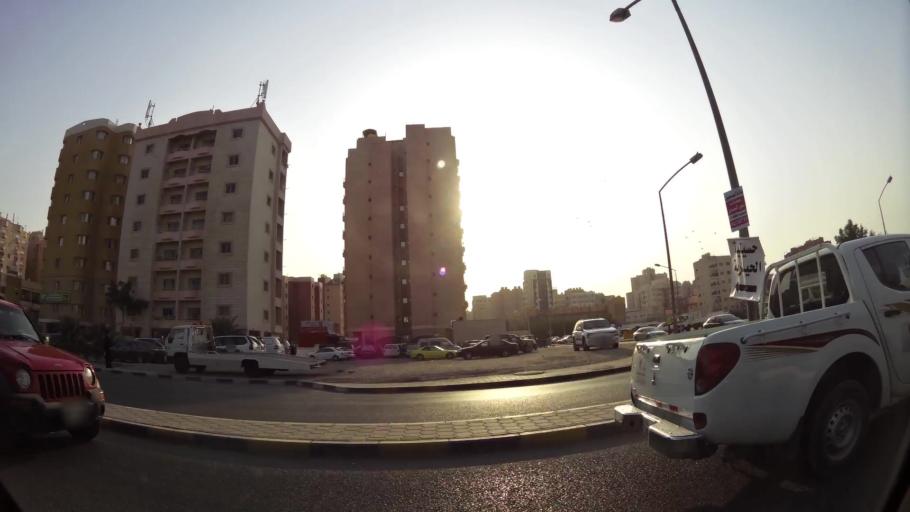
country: KW
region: Muhafazat Hawalli
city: As Salimiyah
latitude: 29.3256
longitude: 48.0644
